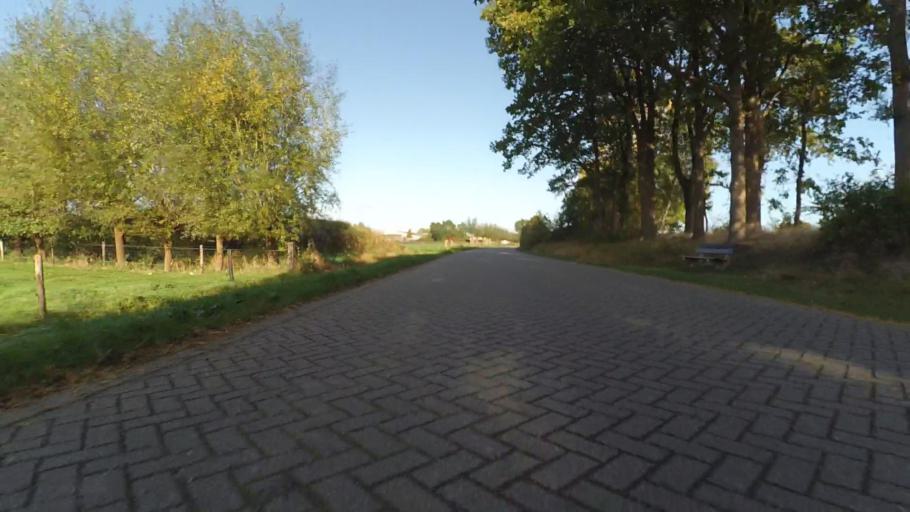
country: NL
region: Gelderland
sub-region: Gemeente Nijkerk
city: Nijkerk
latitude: 52.2542
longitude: 5.5373
